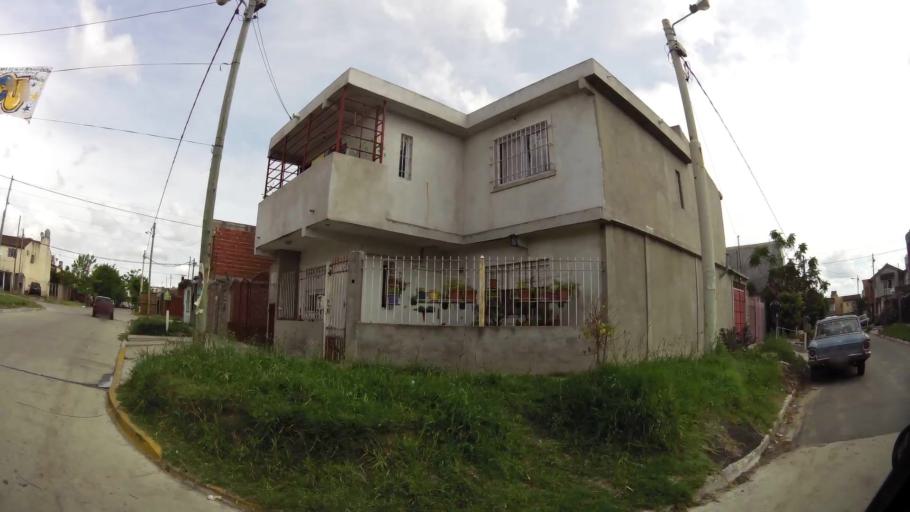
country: AR
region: Buenos Aires
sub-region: Partido de Quilmes
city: Quilmes
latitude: -34.7590
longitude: -58.2493
